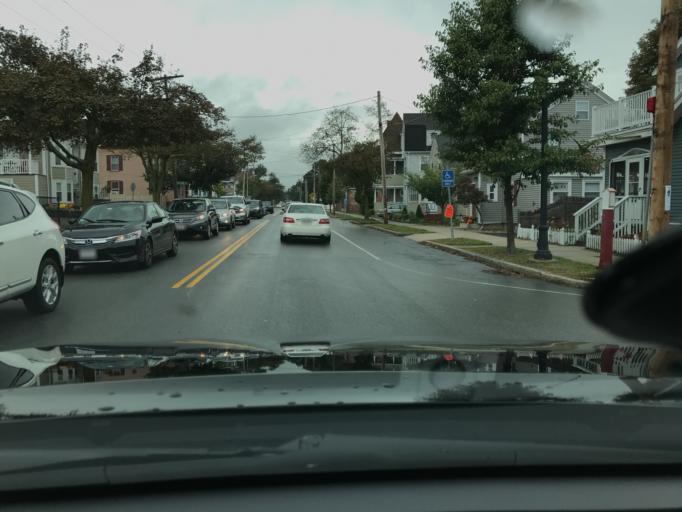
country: US
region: Massachusetts
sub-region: Essex County
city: Salem
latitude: 42.5297
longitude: -70.9061
